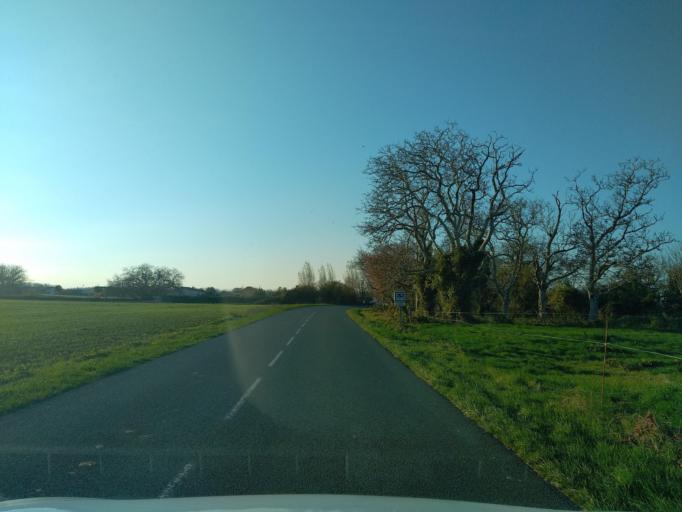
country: FR
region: Pays de la Loire
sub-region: Departement de la Vendee
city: Maillezais
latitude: 46.3406
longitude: -0.7739
